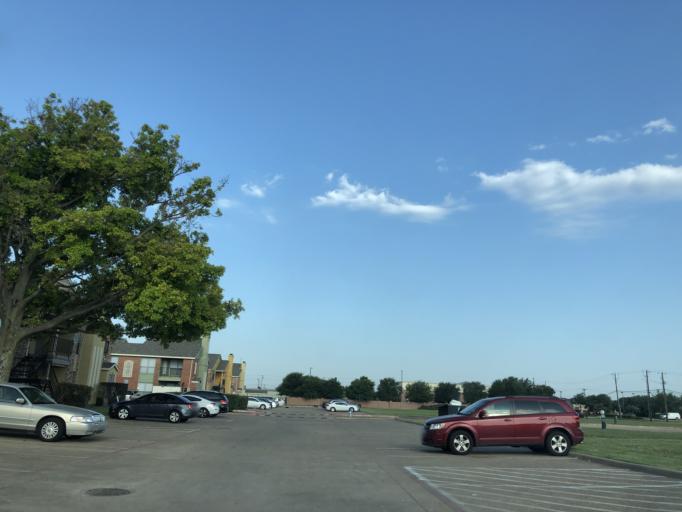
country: US
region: Texas
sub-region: Dallas County
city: Sunnyvale
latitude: 32.8431
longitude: -96.5925
